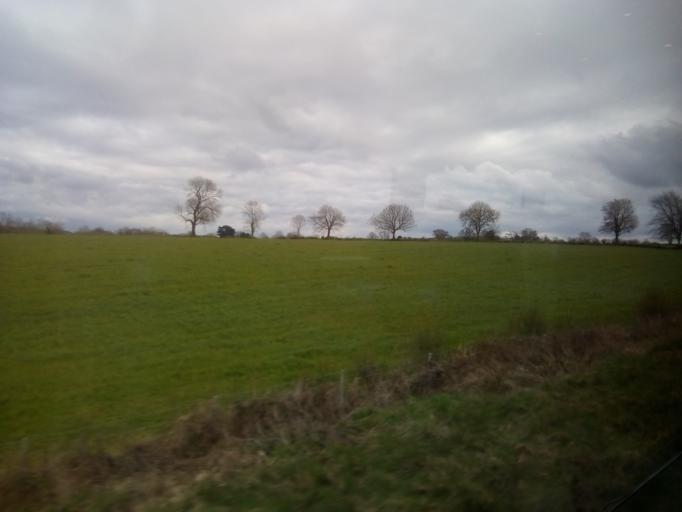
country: IE
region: Leinster
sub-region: An Longfort
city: Longford
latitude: 53.7164
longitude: -7.7543
